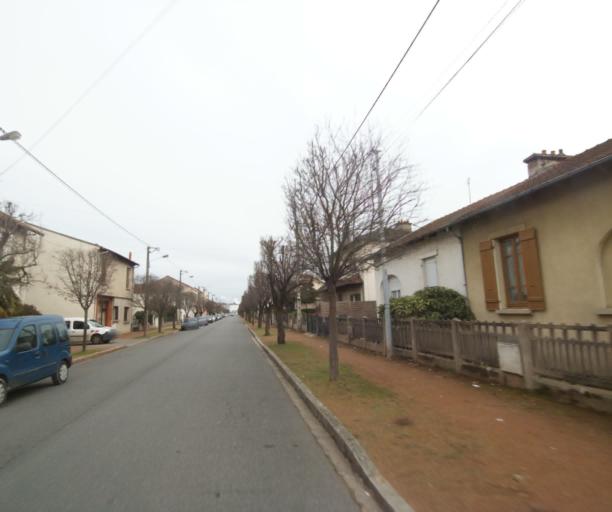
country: FR
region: Rhone-Alpes
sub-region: Departement de la Loire
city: Le Coteau
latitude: 46.0551
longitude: 4.0883
